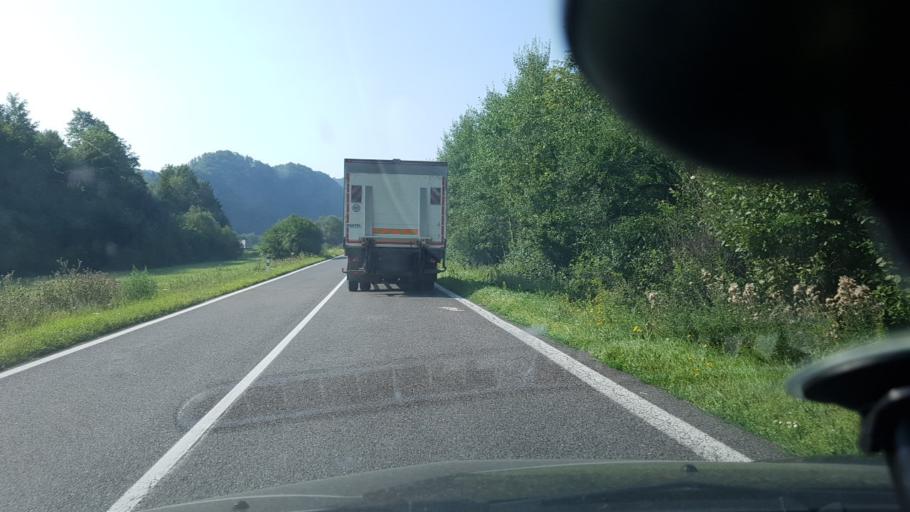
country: SK
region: Zilinsky
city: Tvrdosin
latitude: 49.2784
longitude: 19.4620
